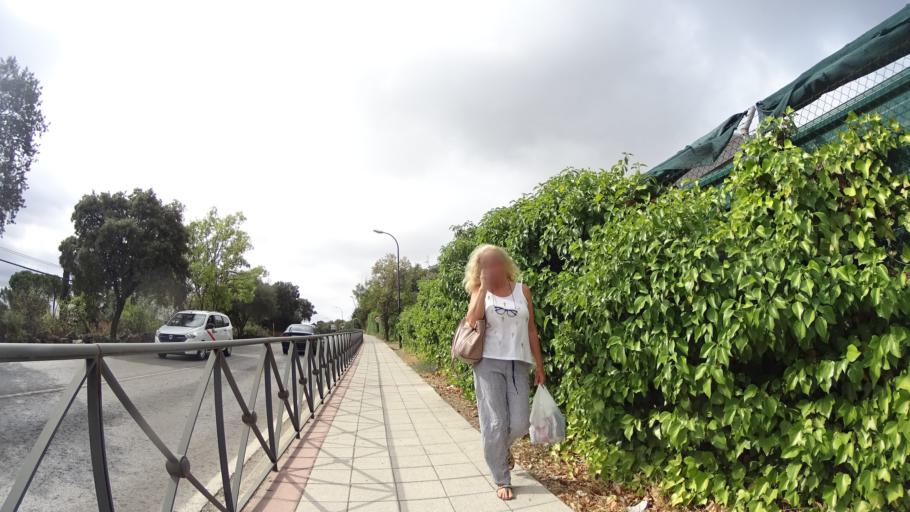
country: ES
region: Madrid
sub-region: Provincia de Madrid
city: Galapagar
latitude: 40.5879
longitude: -4.0119
